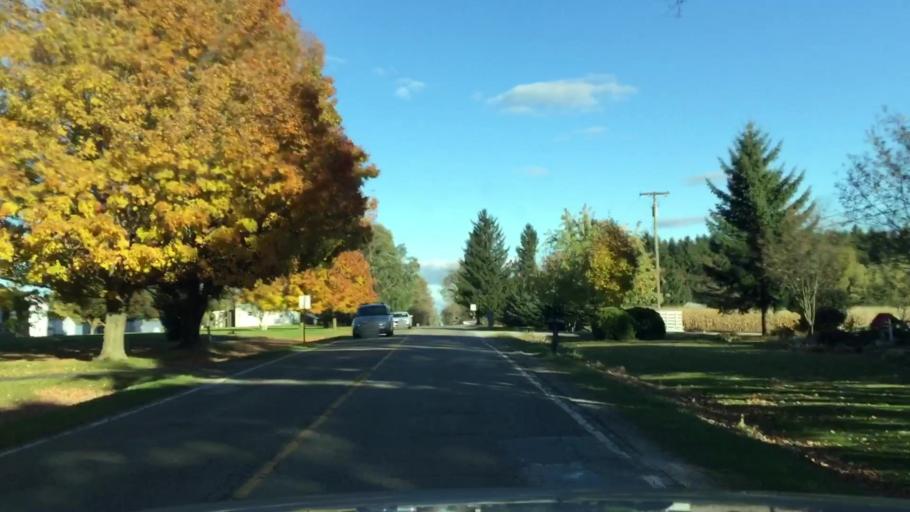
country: US
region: Michigan
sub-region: Lapeer County
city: Lapeer
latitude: 43.0610
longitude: -83.2221
